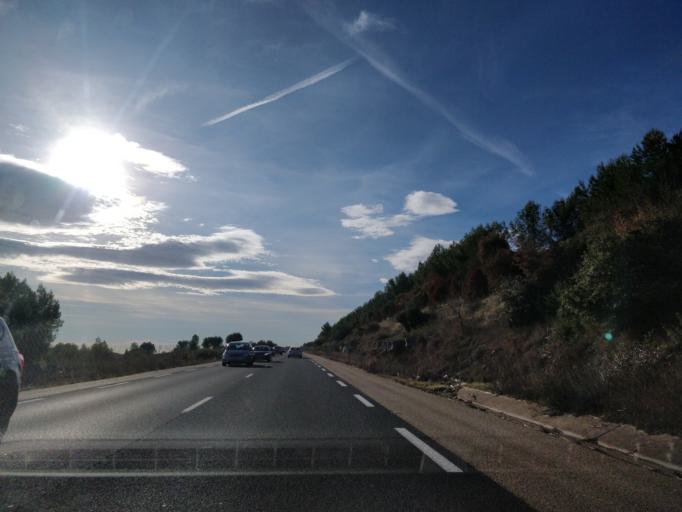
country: FR
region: Languedoc-Roussillon
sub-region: Departement de l'Herault
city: Teyran
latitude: 43.6879
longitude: 3.9440
